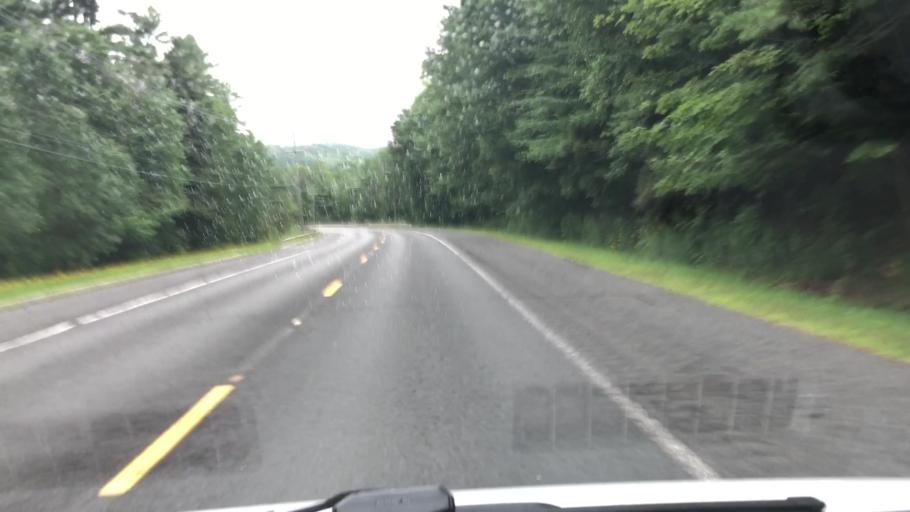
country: US
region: Massachusetts
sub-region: Berkshire County
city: Lanesborough
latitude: 42.5555
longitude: -73.2353
